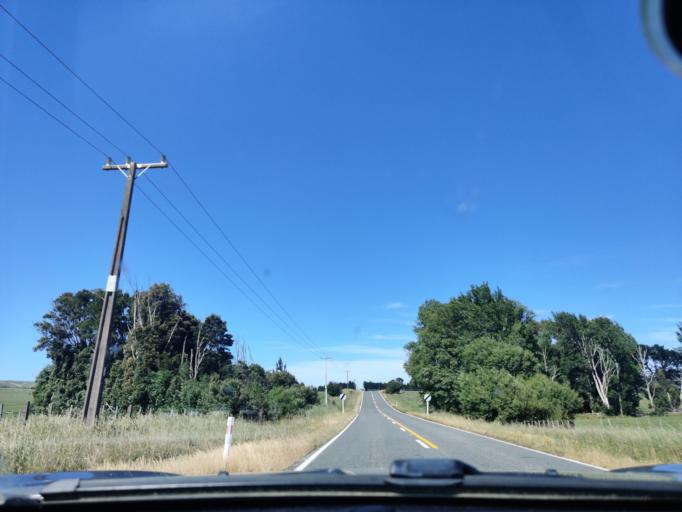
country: NZ
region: Wellington
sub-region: Upper Hutt City
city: Upper Hutt
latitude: -41.3567
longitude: 175.2023
